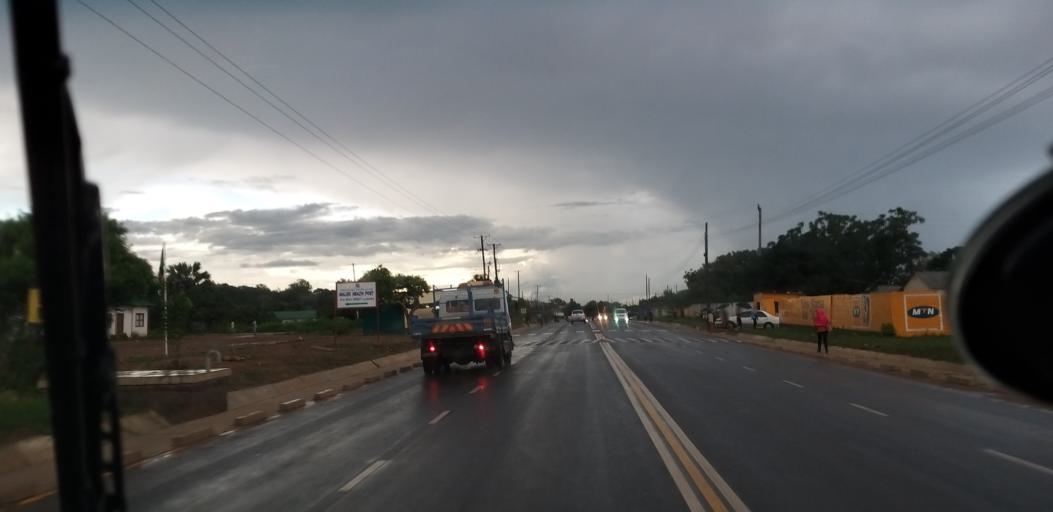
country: ZM
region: Lusaka
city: Lusaka
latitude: -15.4250
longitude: 28.3566
